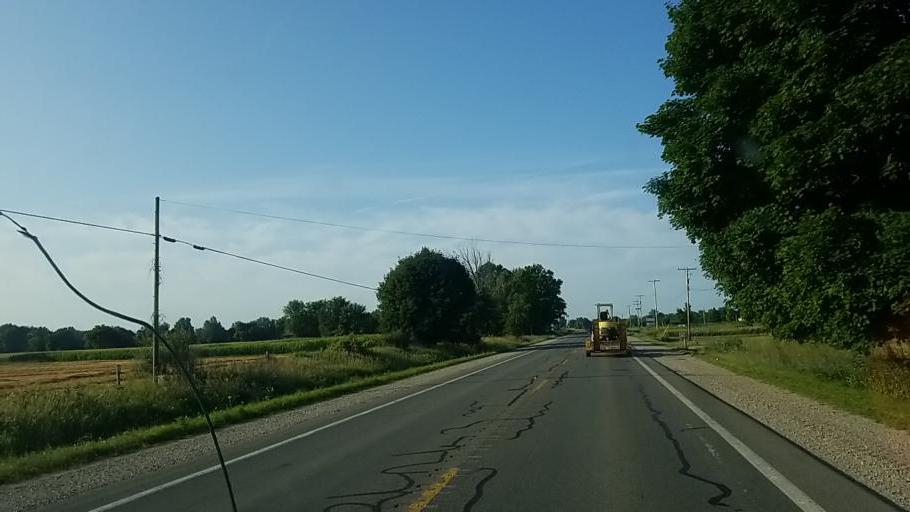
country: US
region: Michigan
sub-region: Montcalm County
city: Stanton
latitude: 43.1990
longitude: -85.0737
